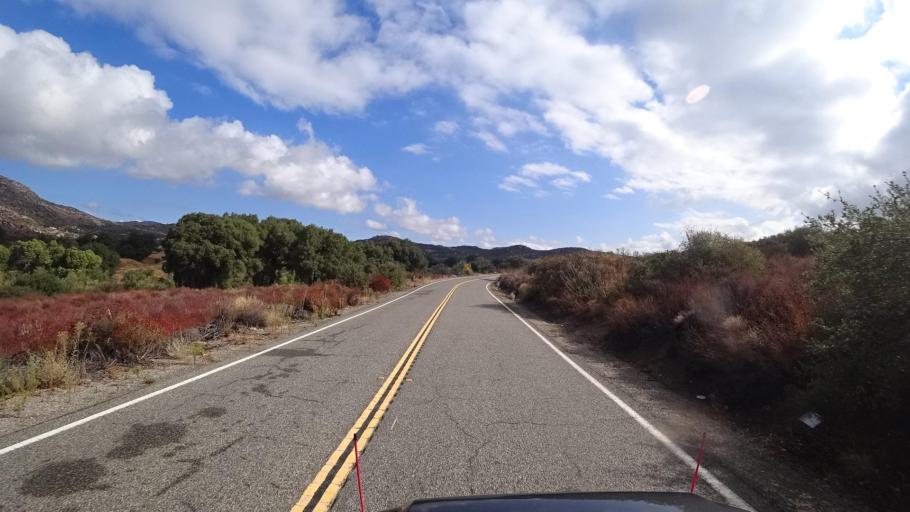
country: US
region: California
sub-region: San Diego County
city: Campo
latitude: 32.5980
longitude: -116.5047
